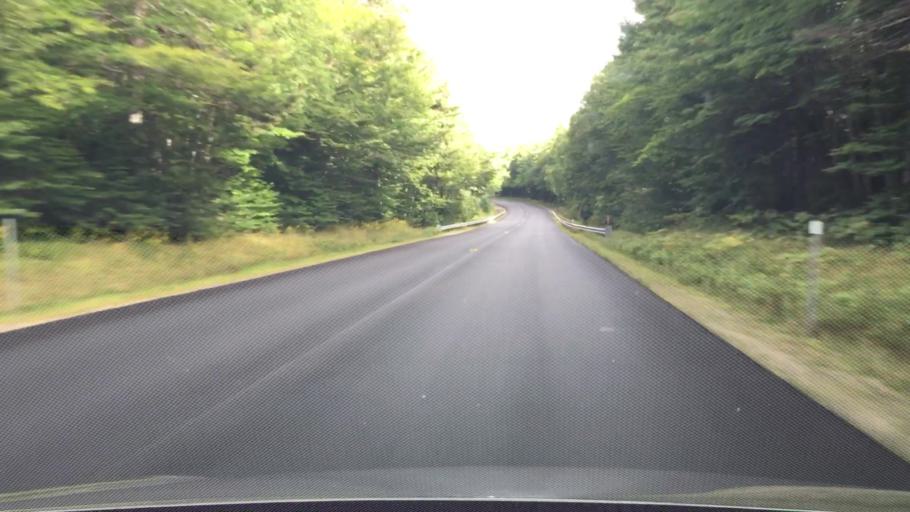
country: US
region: New Hampshire
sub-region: Carroll County
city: Tamworth
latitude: 44.0028
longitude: -71.4154
